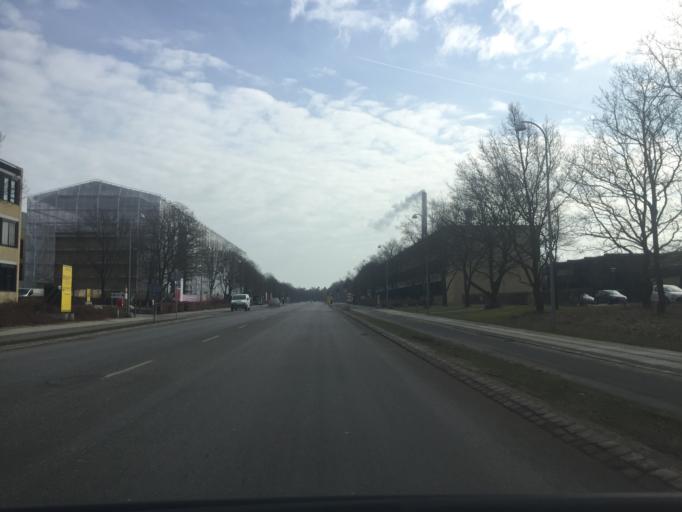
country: DK
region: Capital Region
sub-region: Lyngby-Tarbaek Kommune
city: Kongens Lyngby
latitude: 55.7864
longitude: 12.5179
